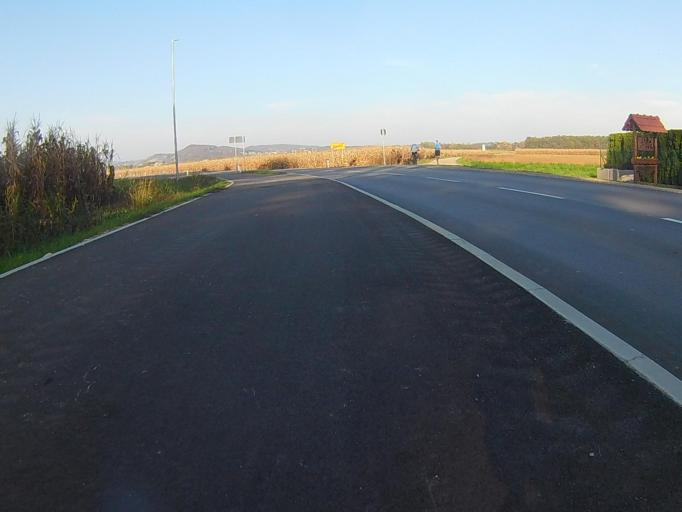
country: SI
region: Miklavz na Dravskem Polju
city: Miklavz na Dravskem Polju
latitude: 46.4877
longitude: 15.7007
